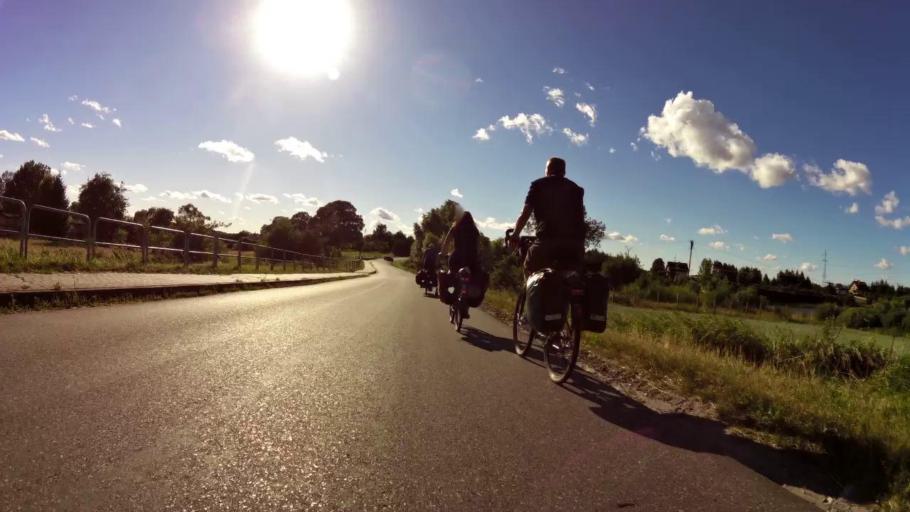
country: PL
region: West Pomeranian Voivodeship
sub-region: Powiat swidwinski
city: Swidwin
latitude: 53.7746
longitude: 15.7574
